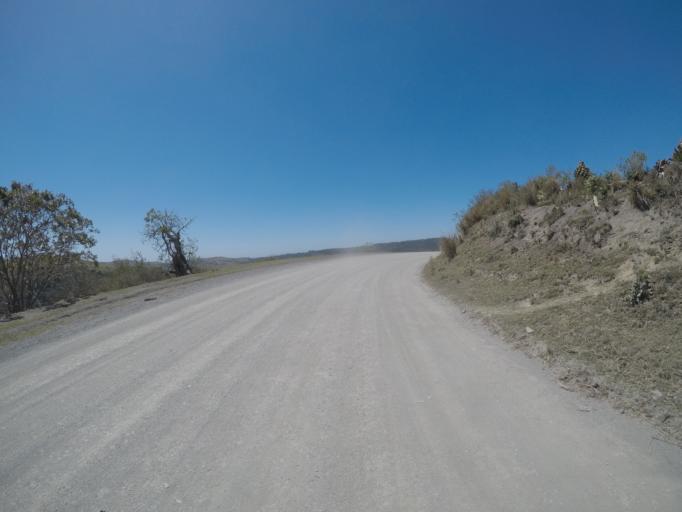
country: ZA
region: Eastern Cape
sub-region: OR Tambo District Municipality
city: Libode
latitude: -31.9975
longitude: 29.0644
